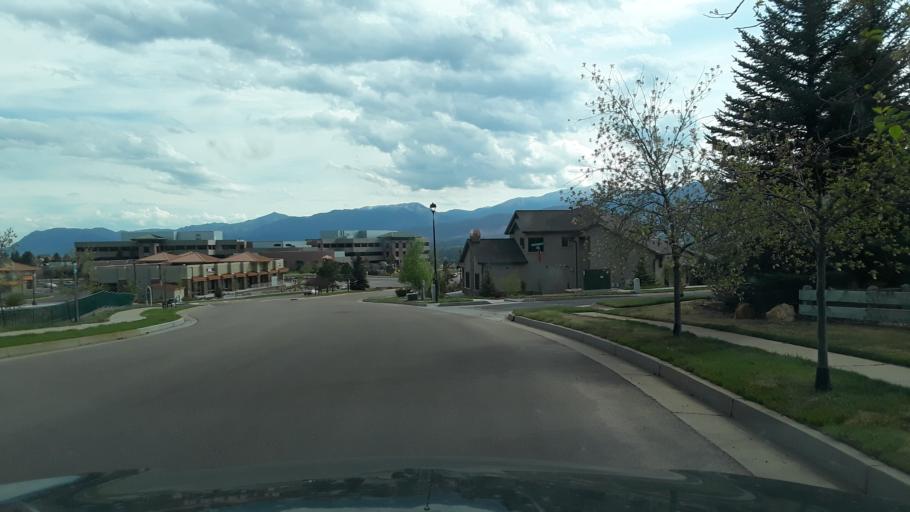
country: US
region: Colorado
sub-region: El Paso County
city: Gleneagle
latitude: 39.0125
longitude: -104.8066
